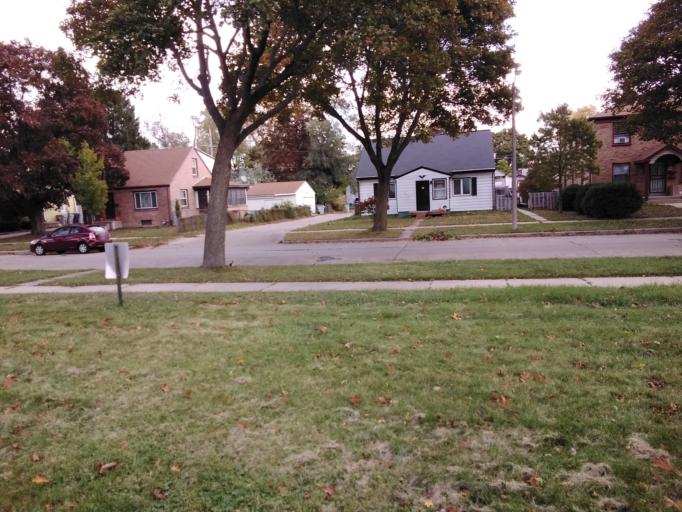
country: US
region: Wisconsin
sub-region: Milwaukee County
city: Glendale
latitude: 43.1228
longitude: -87.9613
